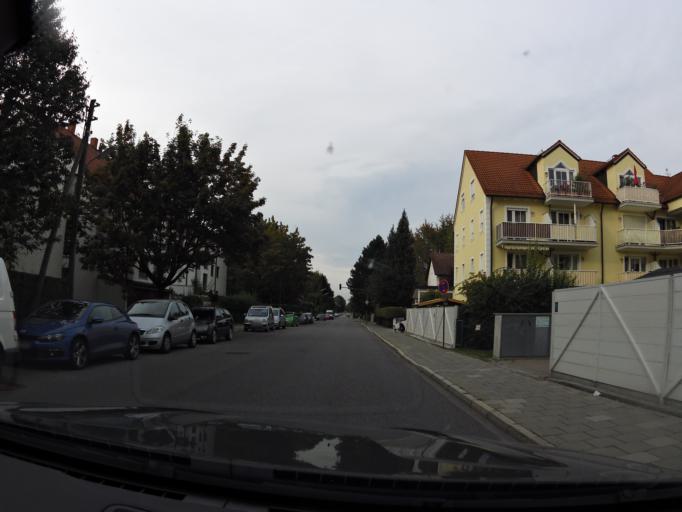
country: DE
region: Bavaria
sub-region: Upper Bavaria
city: Grobenzell
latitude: 48.1805
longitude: 11.3708
